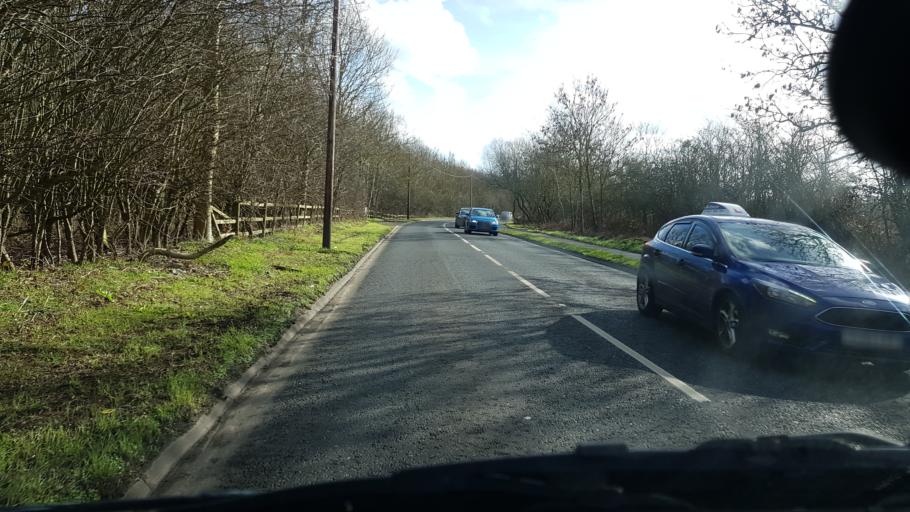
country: GB
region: England
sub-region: Surrey
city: Guildford
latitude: 51.2675
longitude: -0.5567
